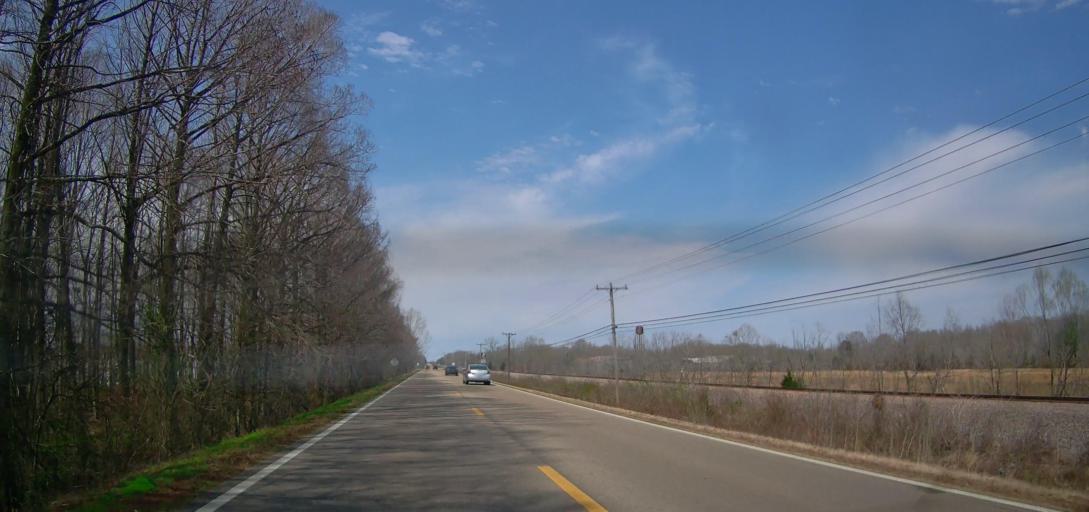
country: US
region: Mississippi
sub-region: Union County
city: New Albany
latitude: 34.5189
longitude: -89.0519
